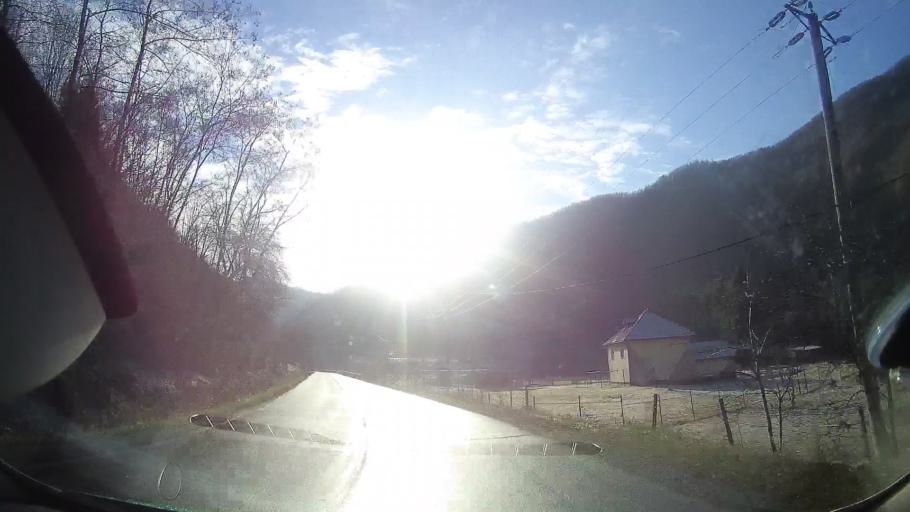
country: RO
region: Alba
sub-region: Comuna Sohodol
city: Sohodol
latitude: 46.3607
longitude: 23.0211
